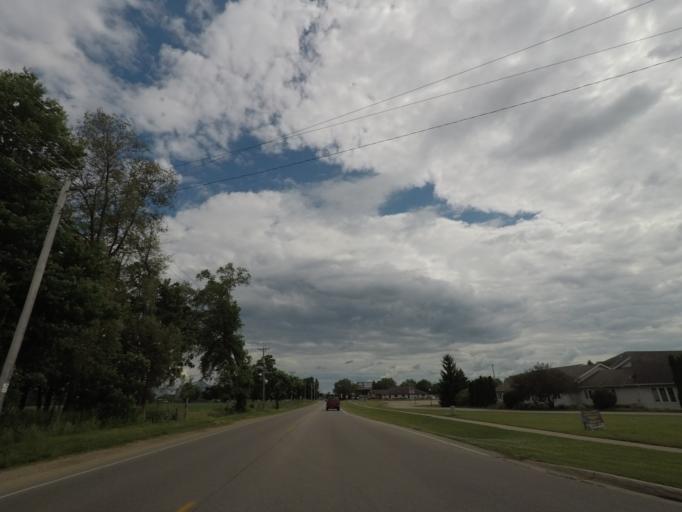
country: US
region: Wisconsin
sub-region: Dane County
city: Belleville
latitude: 42.8742
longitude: -89.5330
